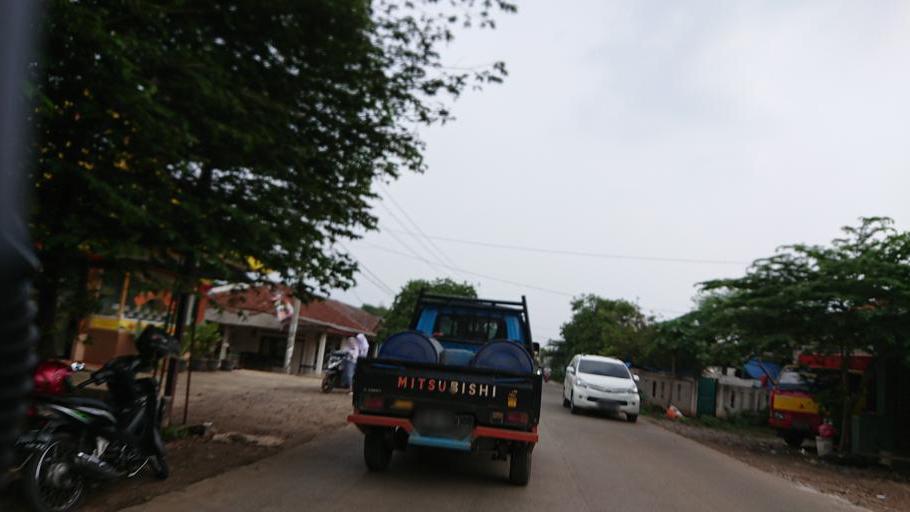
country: ID
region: West Java
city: Parung
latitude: -6.3942
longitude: 106.6851
